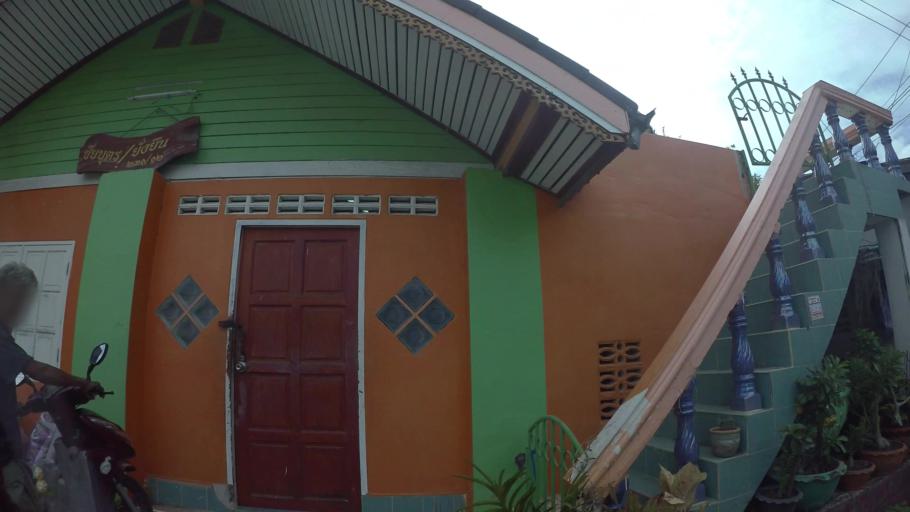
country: TH
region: Rayong
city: Rayong
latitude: 12.6598
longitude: 101.2786
